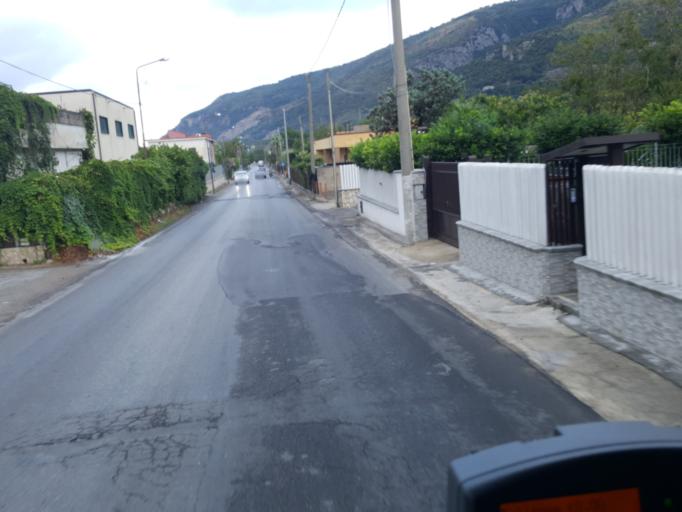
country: IT
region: Campania
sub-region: Provincia di Napoli
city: Striano
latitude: 40.8241
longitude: 14.5984
